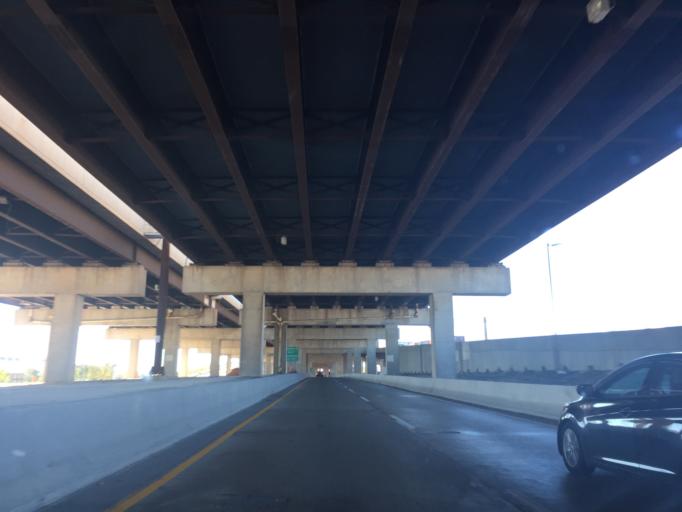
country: US
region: Maryland
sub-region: City of Baltimore
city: Baltimore
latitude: 39.2673
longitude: -76.6058
